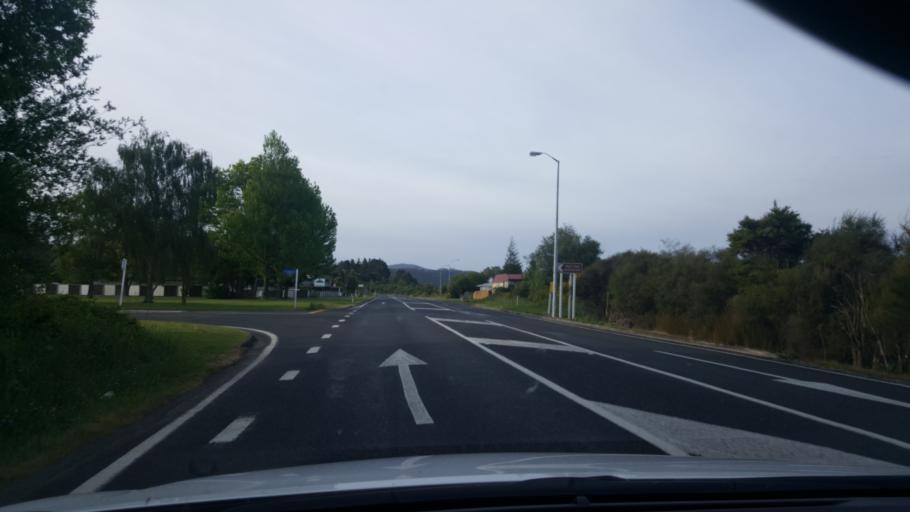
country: NZ
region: Waikato
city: Turangi
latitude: -38.9651
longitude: 175.7666
